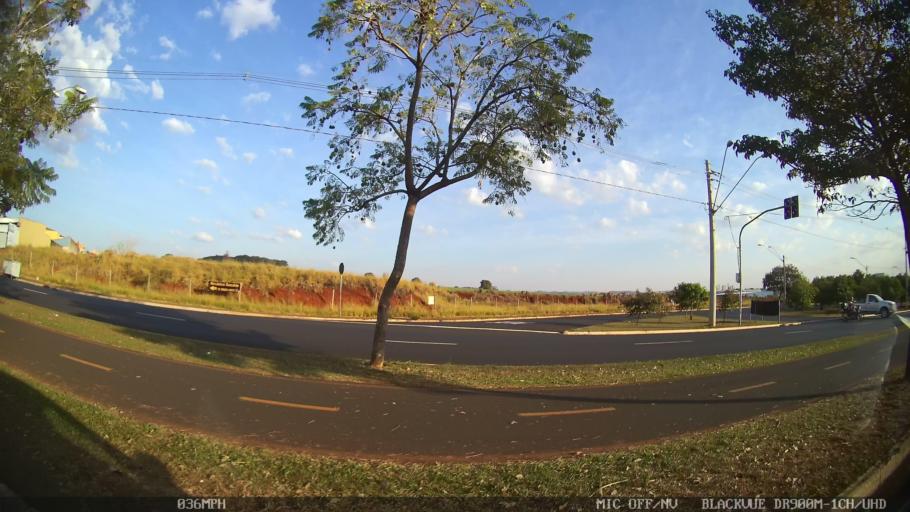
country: BR
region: Sao Paulo
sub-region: Ribeirao Preto
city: Ribeirao Preto
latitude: -21.1935
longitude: -47.7486
